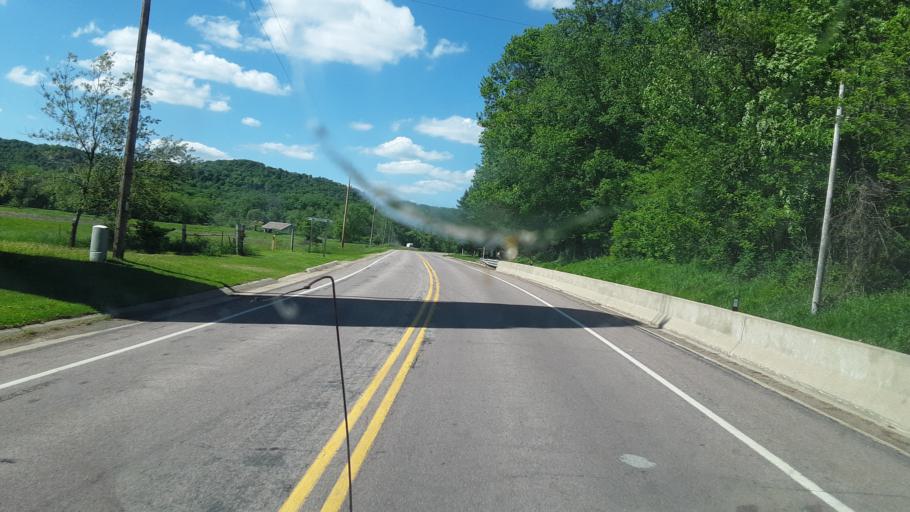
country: US
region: Wisconsin
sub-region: Richland County
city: Richland Center
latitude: 43.3688
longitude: -90.2661
